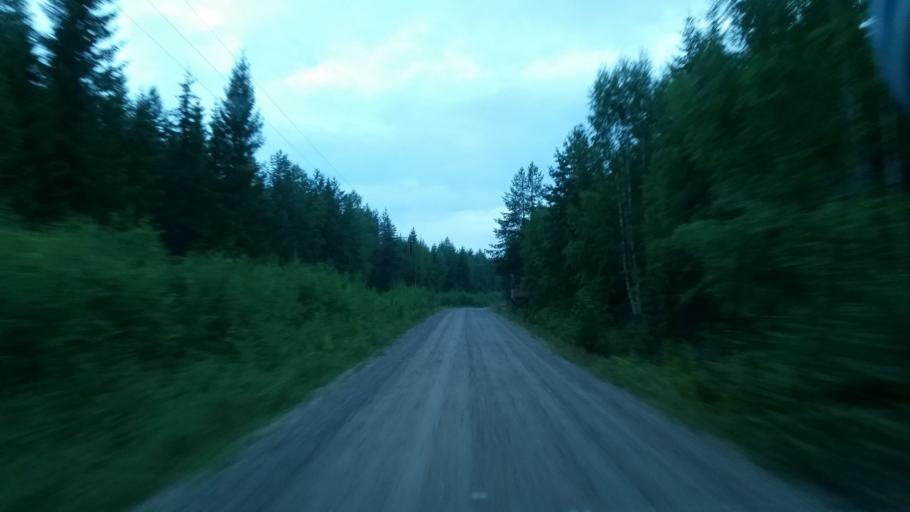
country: SE
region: Gaevleborg
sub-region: Ljusdals Kommun
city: Farila
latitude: 61.9162
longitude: 15.8359
